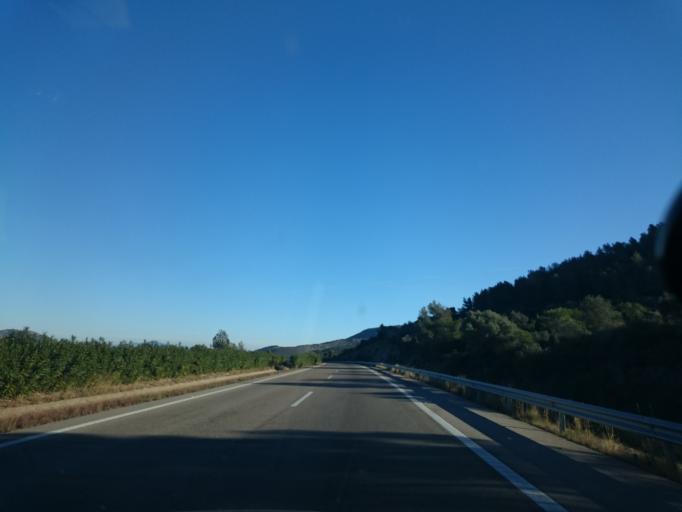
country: ES
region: Valencia
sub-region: Provincia de Castello
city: Santa Magdalena de Pulpis
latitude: 40.3552
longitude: 0.3134
